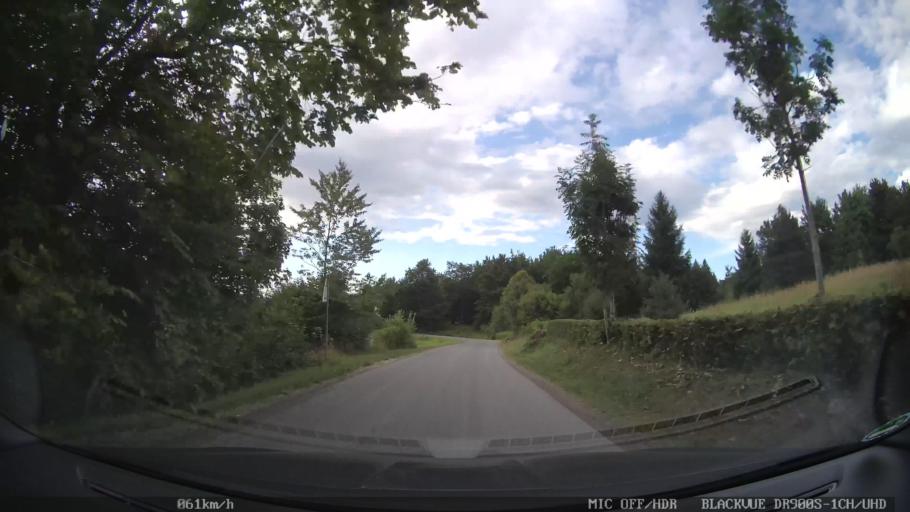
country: HR
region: Licko-Senjska
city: Jezerce
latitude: 44.9436
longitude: 15.5413
